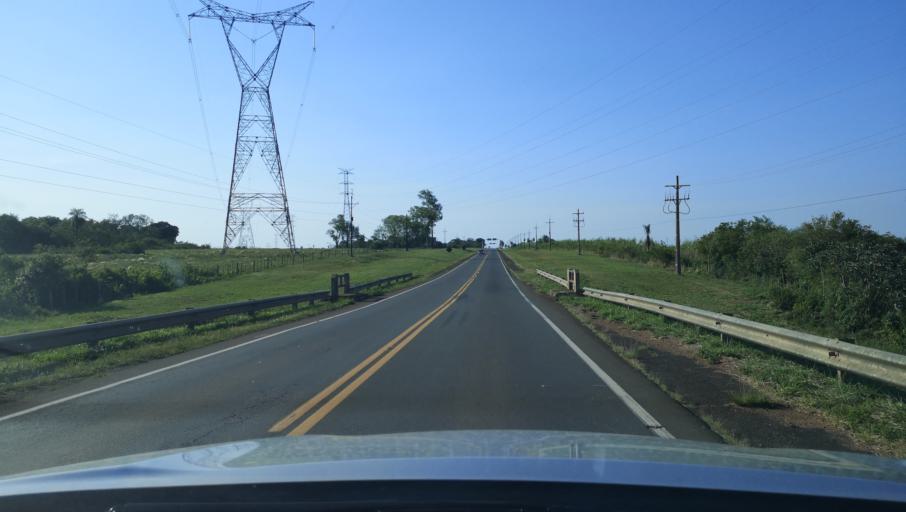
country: PY
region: Misiones
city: Santa Maria
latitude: -26.7896
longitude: -57.0250
